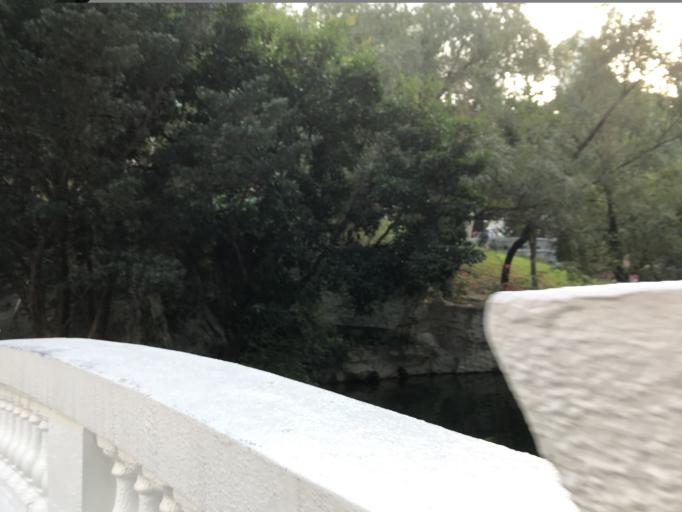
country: HK
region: Central and Western
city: Central
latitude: 22.2776
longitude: 114.1618
